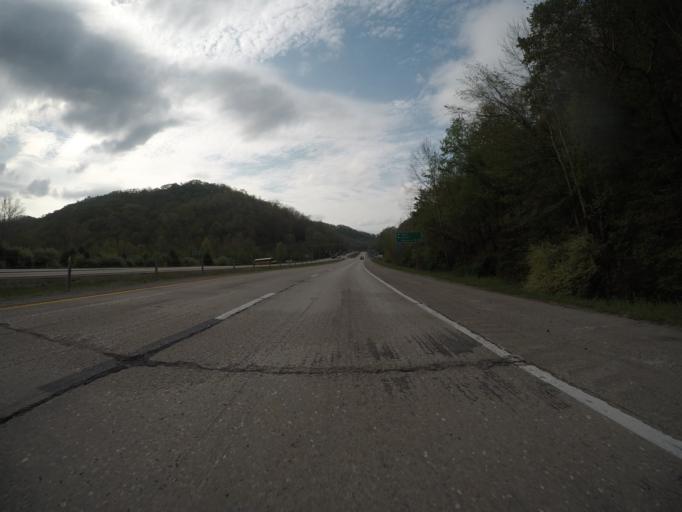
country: US
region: West Virginia
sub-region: Boone County
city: Madison
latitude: 38.0998
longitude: -81.8393
